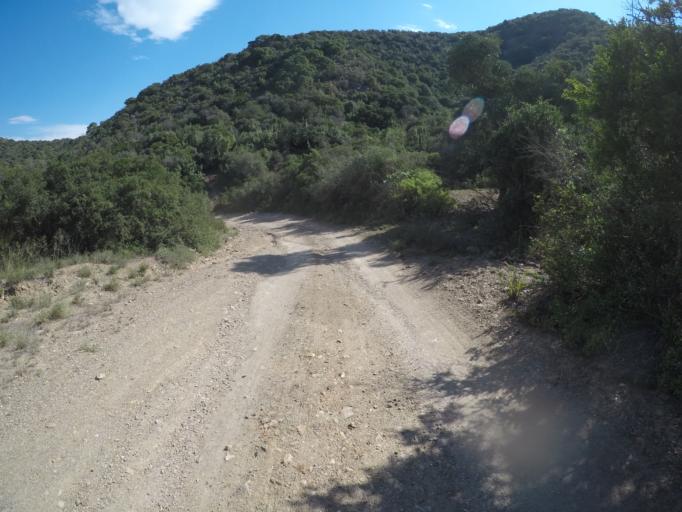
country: ZA
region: Eastern Cape
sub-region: Cacadu District Municipality
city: Kareedouw
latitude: -33.6545
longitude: 24.4031
